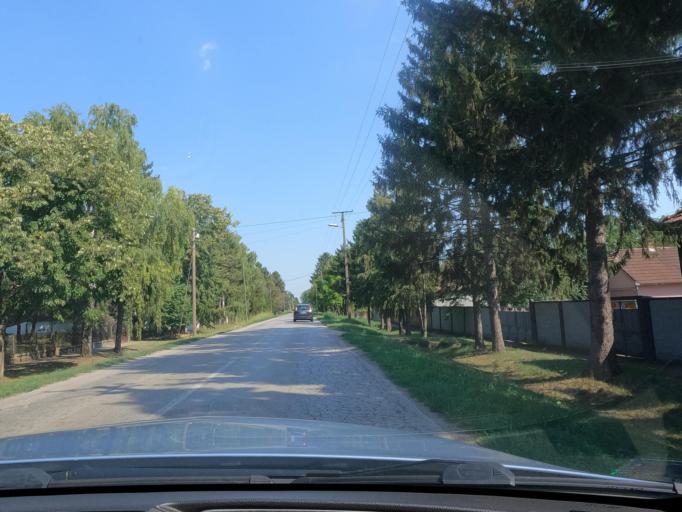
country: RS
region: Autonomna Pokrajina Vojvodina
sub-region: Severnobacki Okrug
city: Mali Igos
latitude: 45.7617
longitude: 19.7544
